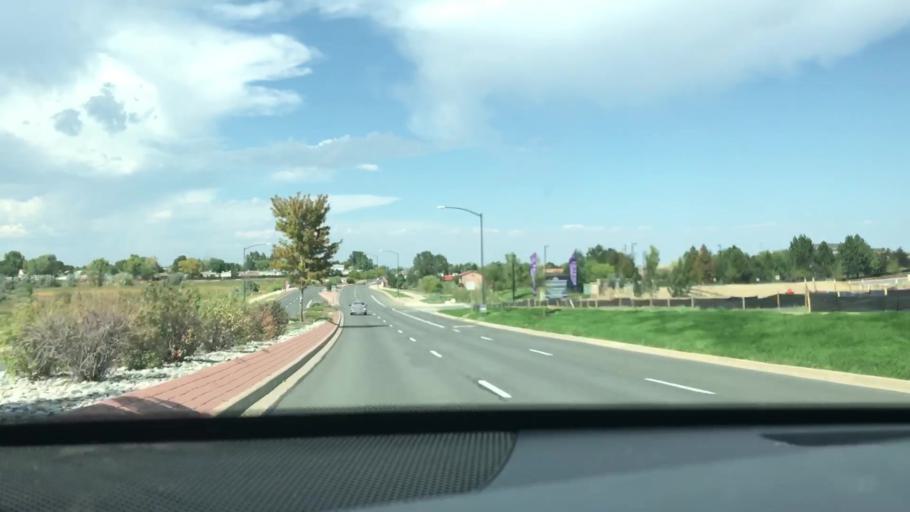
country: US
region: Colorado
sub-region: Adams County
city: Northglenn
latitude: 39.9312
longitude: -104.9968
